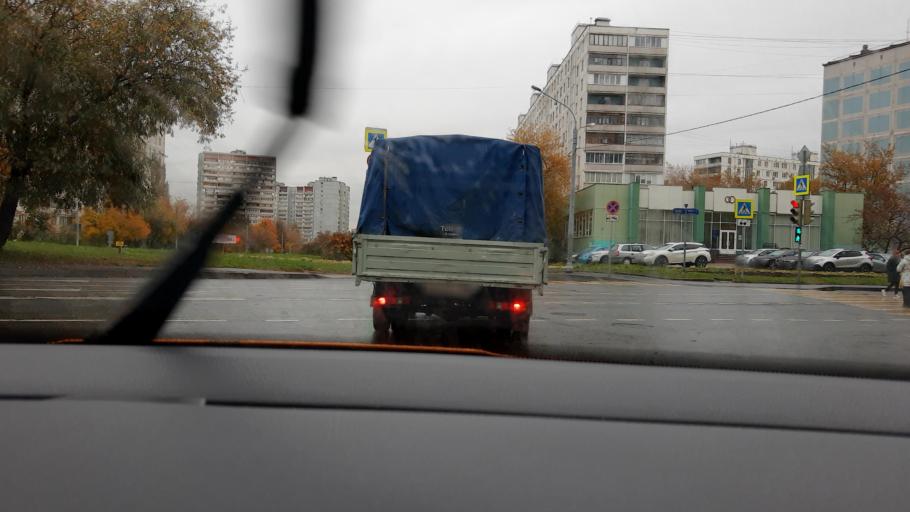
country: RU
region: Moscow
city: Leonovo
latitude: 55.8774
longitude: 37.6445
